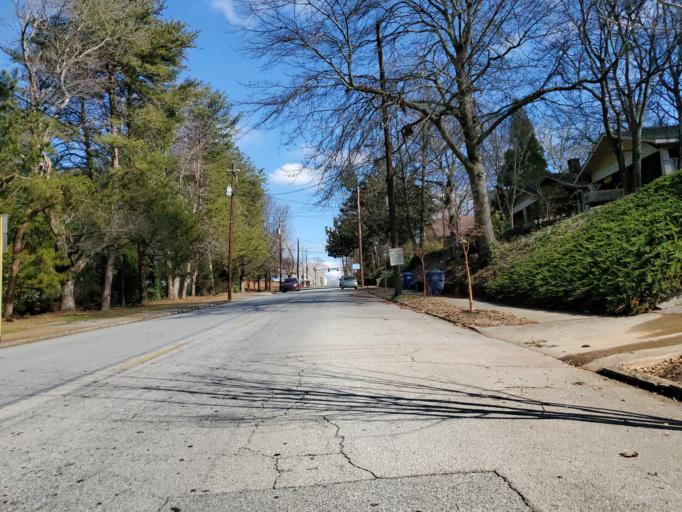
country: US
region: Georgia
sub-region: Fulton County
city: Atlanta
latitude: 33.7302
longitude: -84.3702
